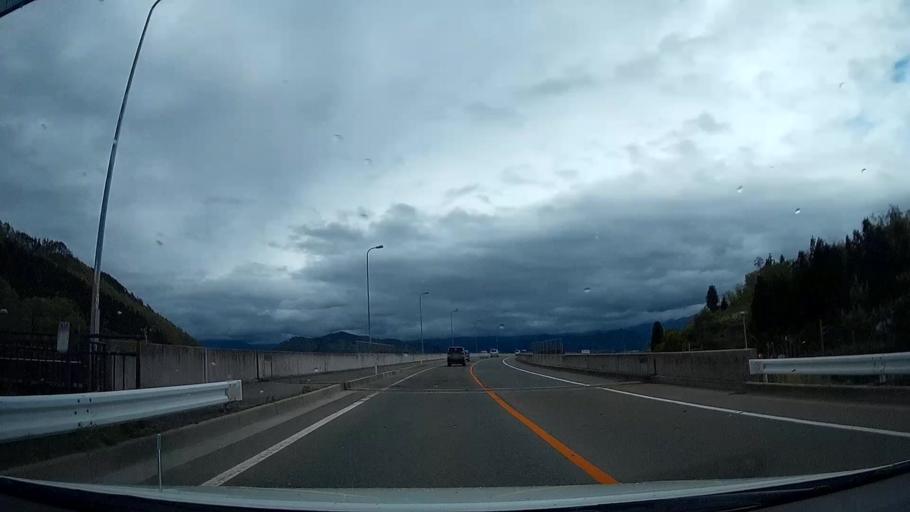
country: JP
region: Yamagata
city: Kaminoyama
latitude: 38.1307
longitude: 140.2462
